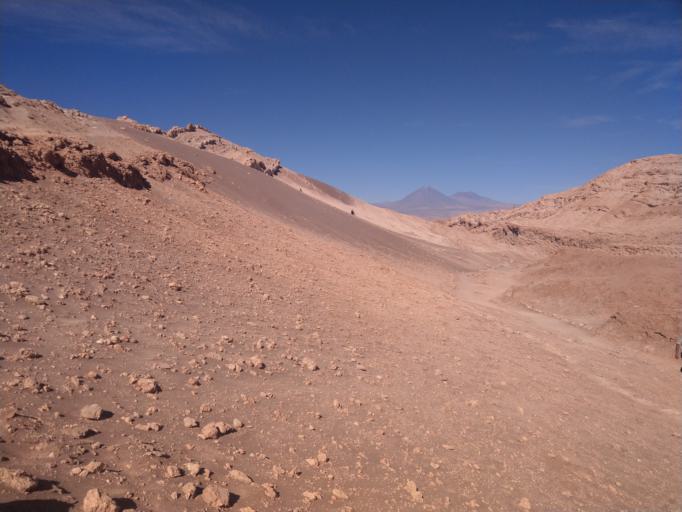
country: CL
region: Antofagasta
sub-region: Provincia de El Loa
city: San Pedro de Atacama
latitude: -22.9493
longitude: -68.2984
